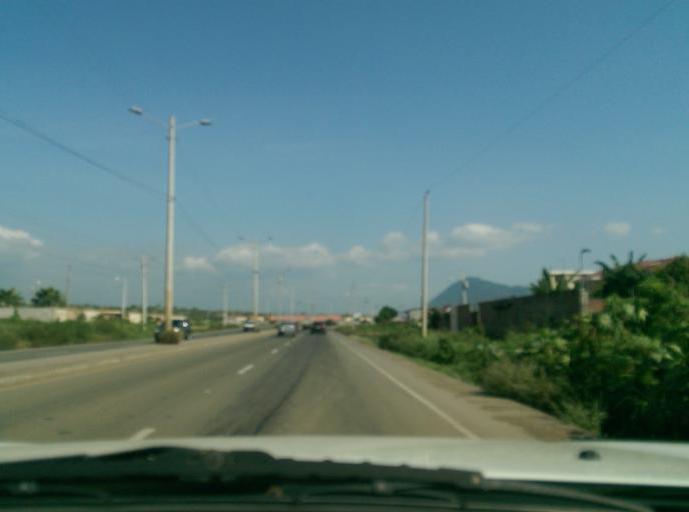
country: EC
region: Manabi
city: Manta
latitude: -0.9847
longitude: -80.6763
